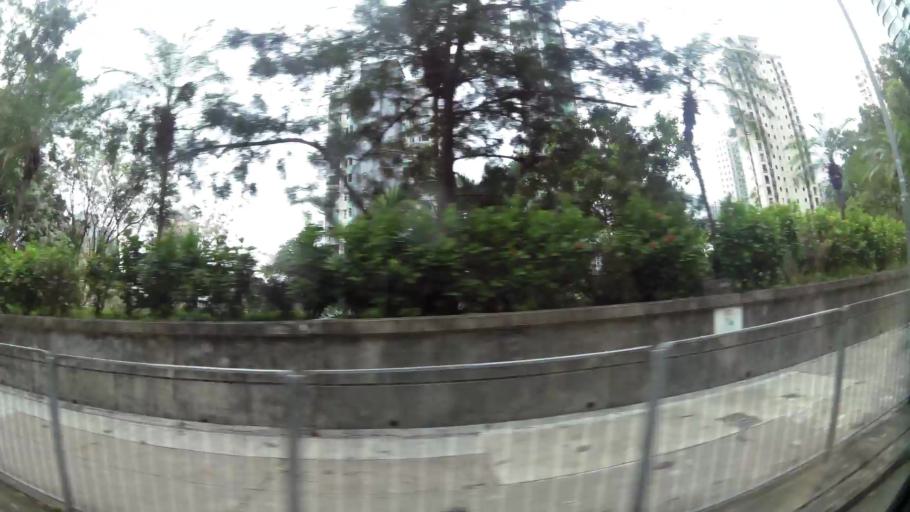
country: HK
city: Hong Kong
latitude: 22.2832
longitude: 114.1479
